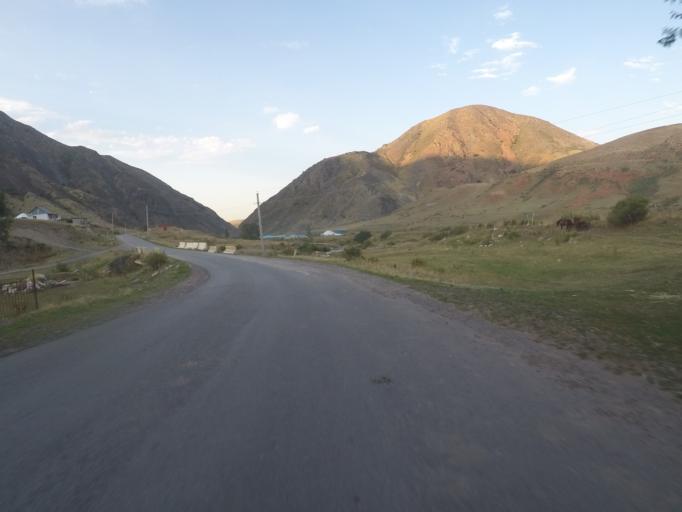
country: KG
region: Chuy
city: Bishkek
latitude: 42.6748
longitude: 74.6533
